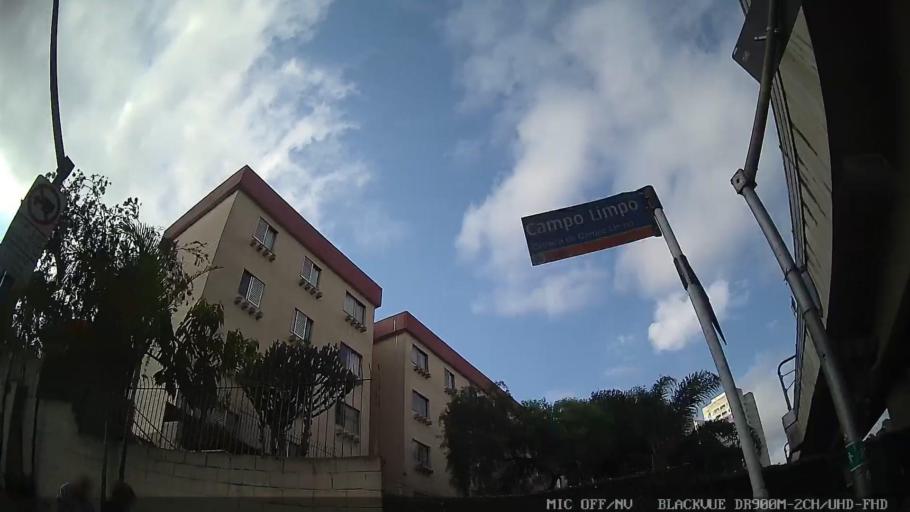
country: BR
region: Sao Paulo
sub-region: Taboao Da Serra
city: Taboao da Serra
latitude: -23.6484
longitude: -46.7585
